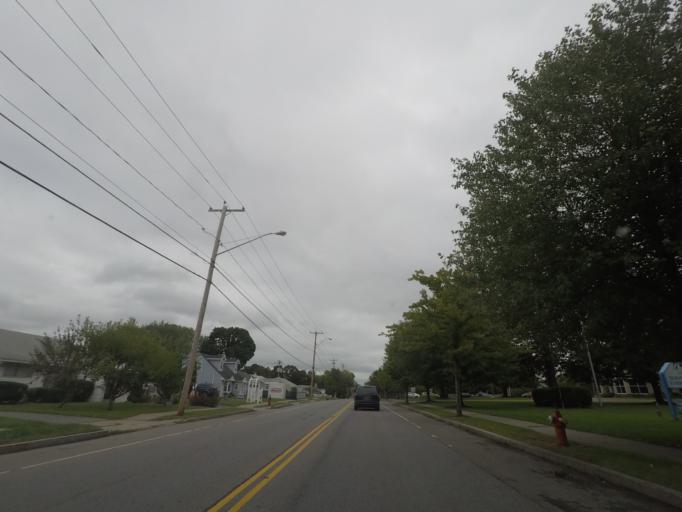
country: US
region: New York
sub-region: Albany County
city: Delmar
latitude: 42.6493
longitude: -73.8069
